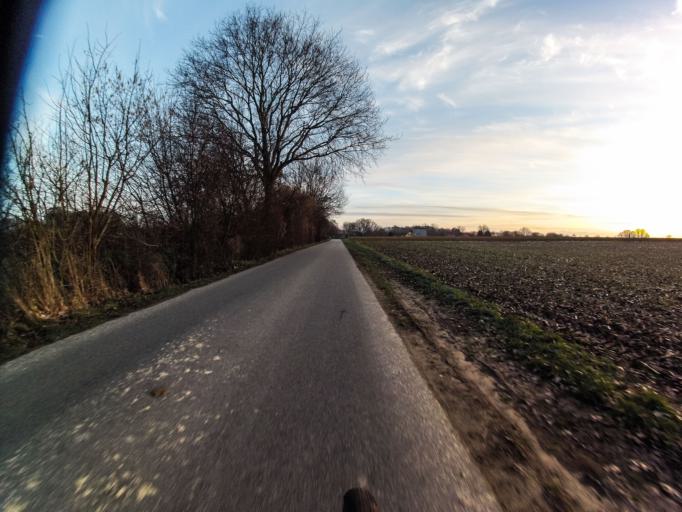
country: DE
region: North Rhine-Westphalia
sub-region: Regierungsbezirk Munster
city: Westerkappeln
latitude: 52.2761
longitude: 7.8411
